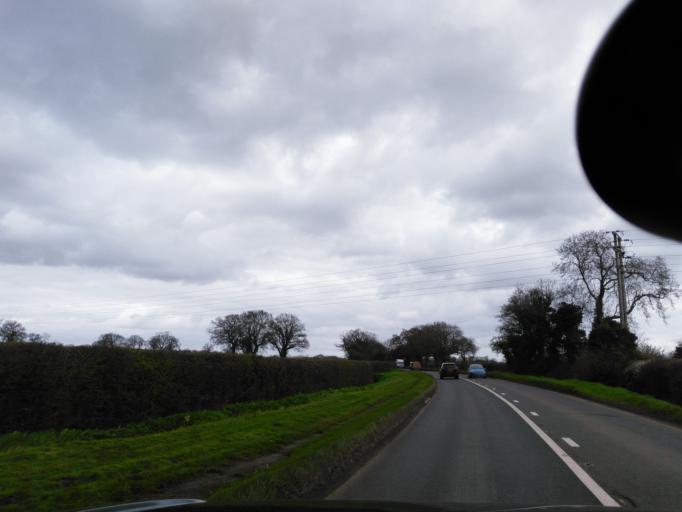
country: GB
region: England
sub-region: Wiltshire
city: Malmesbury
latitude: 51.5611
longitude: -2.1037
